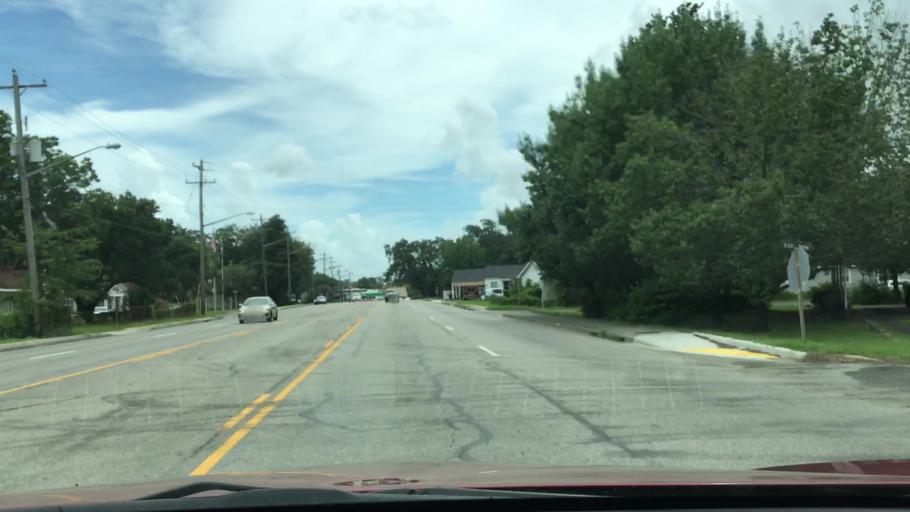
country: US
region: South Carolina
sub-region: Georgetown County
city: Georgetown
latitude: 33.3781
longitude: -79.2877
